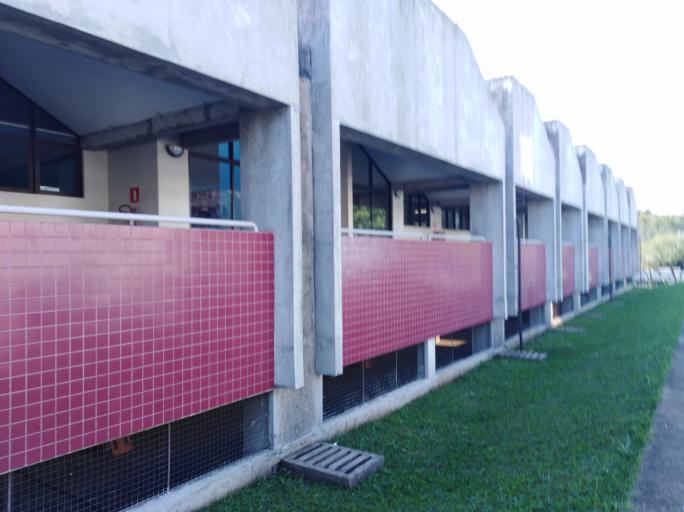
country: BR
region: Parana
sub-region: Curitiba
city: Curitiba
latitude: -25.4452
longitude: -49.2388
